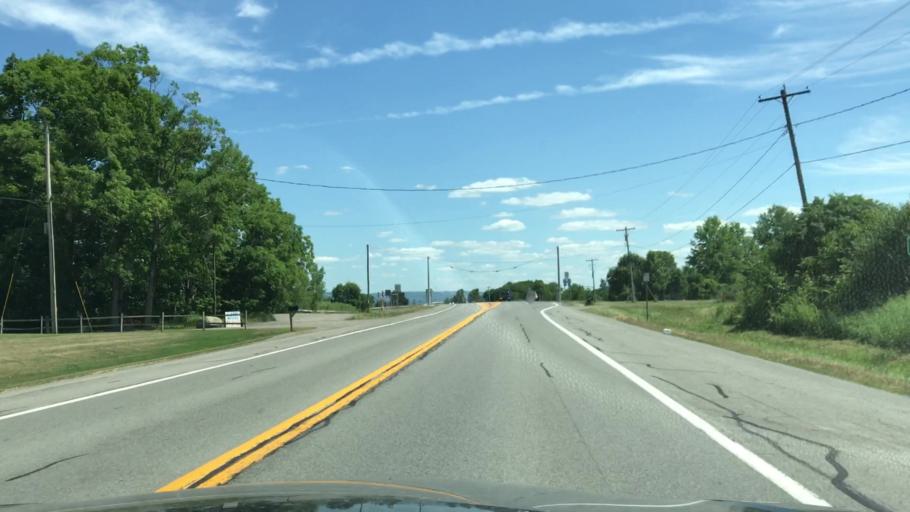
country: US
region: New York
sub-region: Livingston County
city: Mount Morris
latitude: 42.6733
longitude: -77.8141
